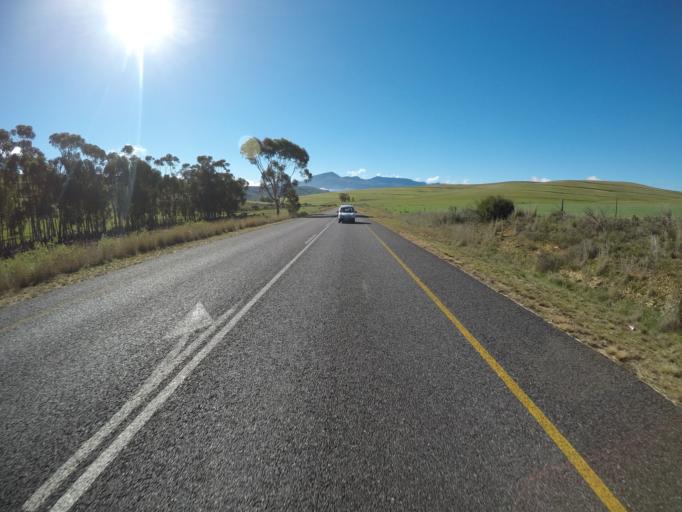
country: ZA
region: Western Cape
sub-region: Overberg District Municipality
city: Caledon
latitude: -34.1138
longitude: 19.5227
